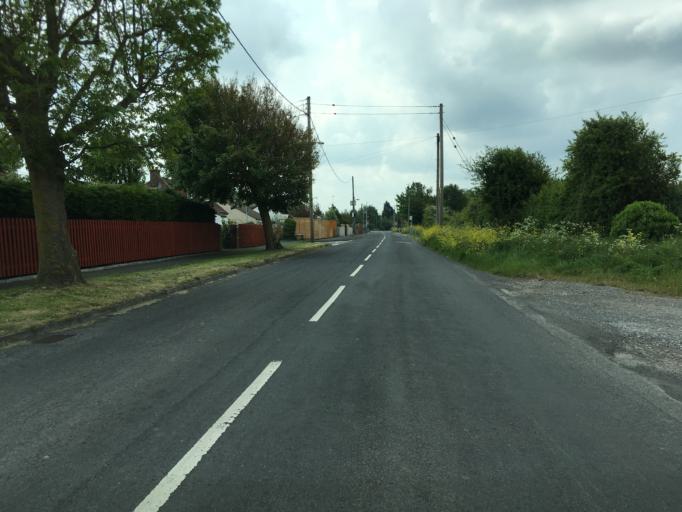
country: GB
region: England
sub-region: South Gloucestershire
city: Severn Beach
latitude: 51.5561
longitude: -2.6605
